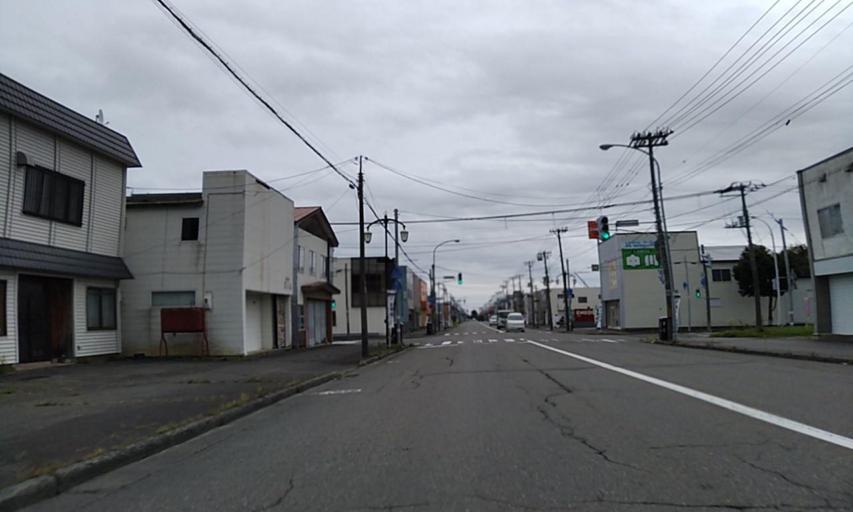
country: JP
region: Hokkaido
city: Obihiro
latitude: 42.2907
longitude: 143.3139
